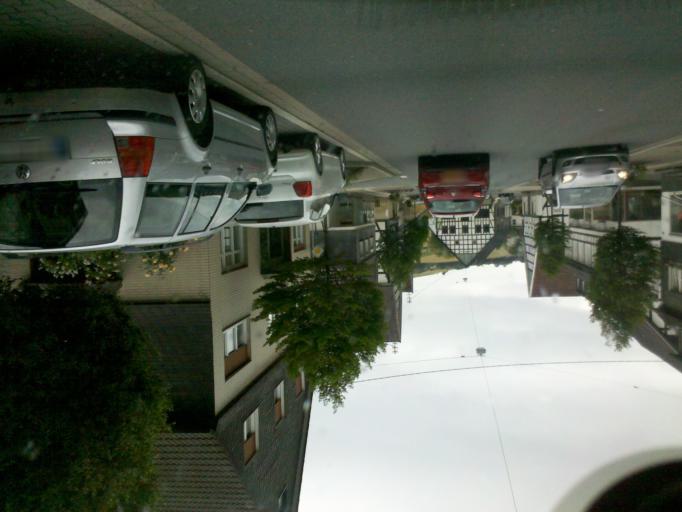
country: DE
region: North Rhine-Westphalia
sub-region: Regierungsbezirk Arnsberg
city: Lennestadt
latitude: 51.1543
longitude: 8.0560
